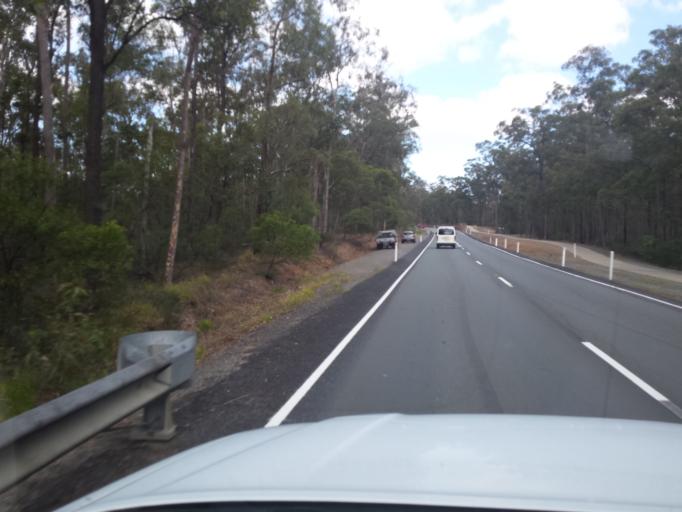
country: AU
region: Queensland
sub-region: Moreton Bay
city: Ferny Hills
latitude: -27.3738
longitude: 152.9601
